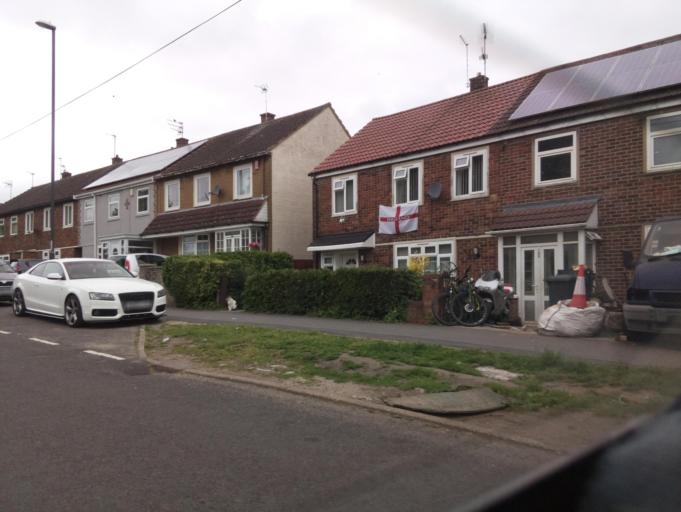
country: GB
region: England
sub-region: Derby
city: Derby
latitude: 52.9270
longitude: -1.5223
